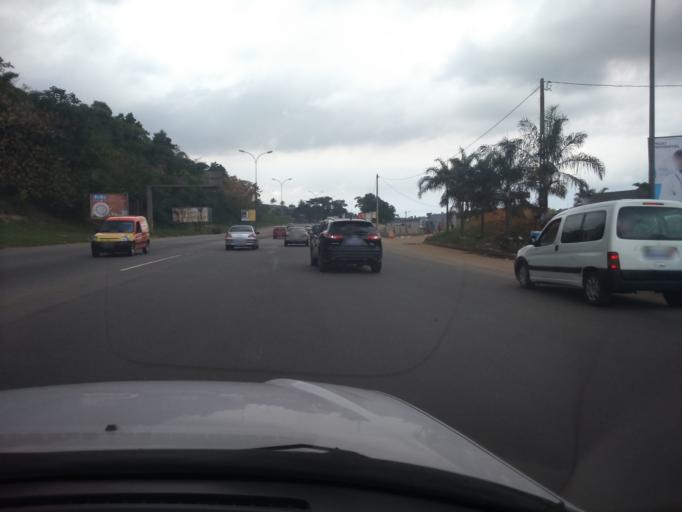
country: CI
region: Lagunes
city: Abidjan
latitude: 5.3577
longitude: -4.0404
